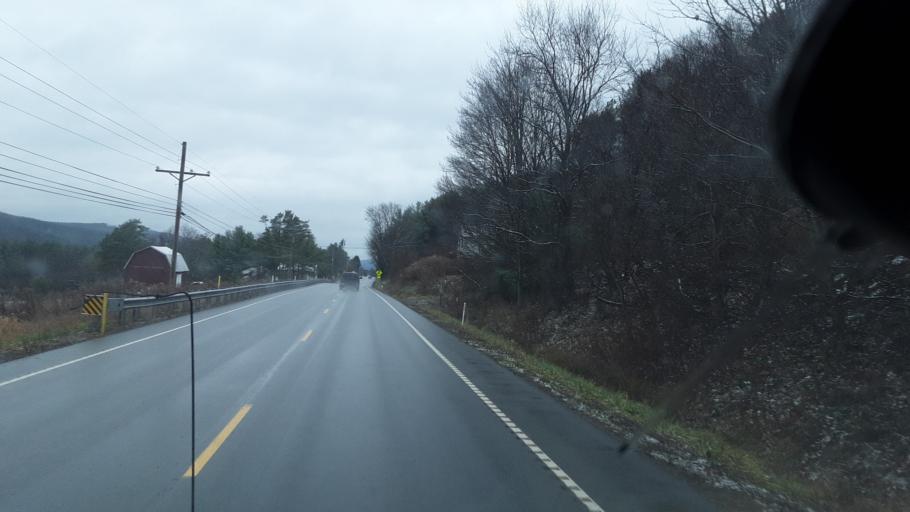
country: US
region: Pennsylvania
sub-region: Potter County
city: Shinglehouse
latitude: 41.9489
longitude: -78.1641
